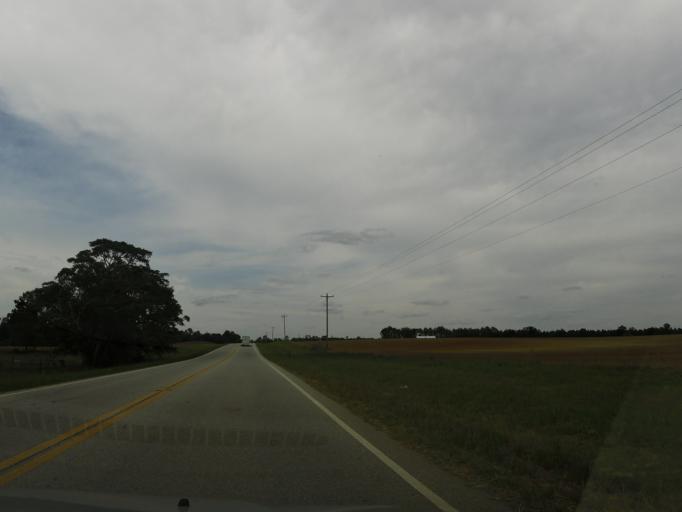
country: US
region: Georgia
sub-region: Emanuel County
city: Twin City
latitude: 32.4859
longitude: -82.2456
